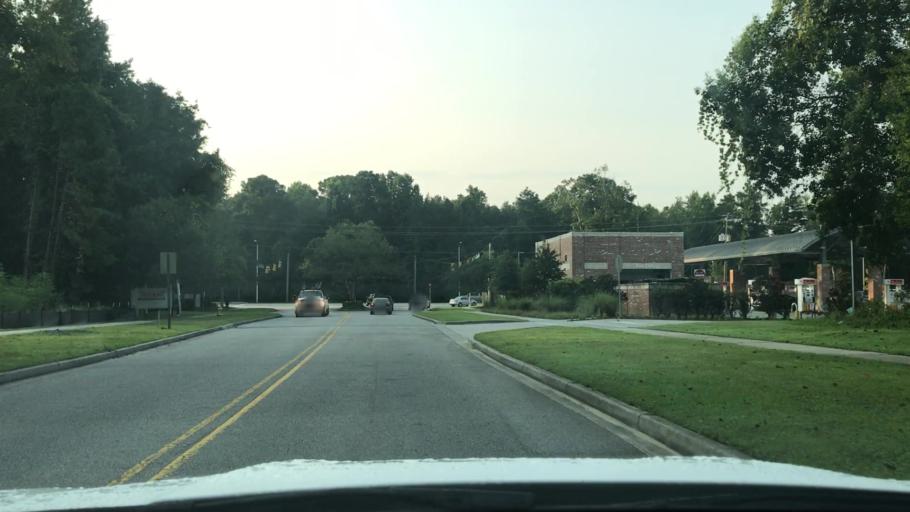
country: US
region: South Carolina
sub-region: Charleston County
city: Shell Point
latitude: 32.8251
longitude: -80.0856
